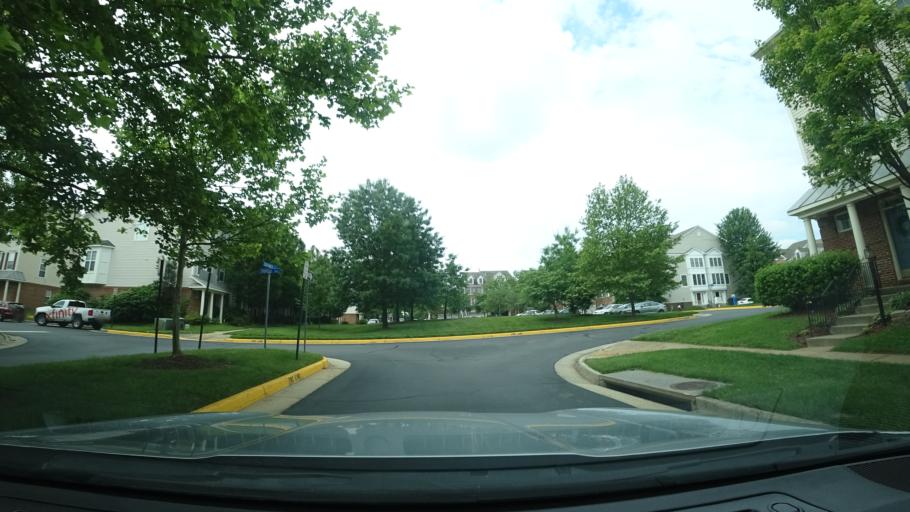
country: US
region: Virginia
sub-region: Loudoun County
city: Countryside
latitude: 39.0385
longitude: -77.4005
